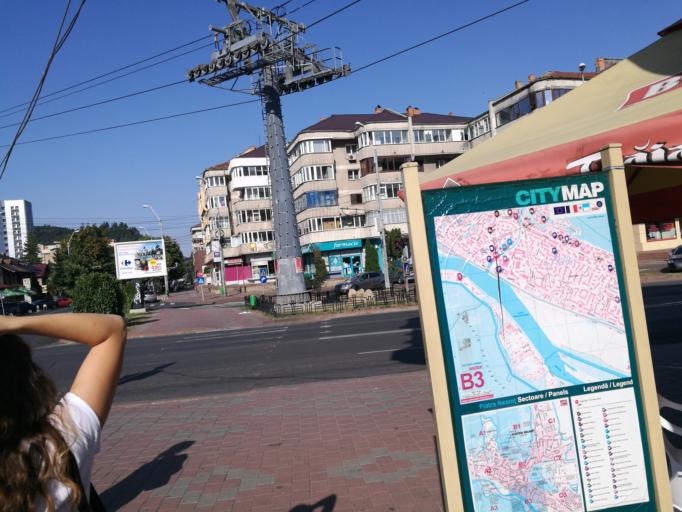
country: RO
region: Neamt
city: Piatra Neamt
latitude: 46.9276
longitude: 26.3613
